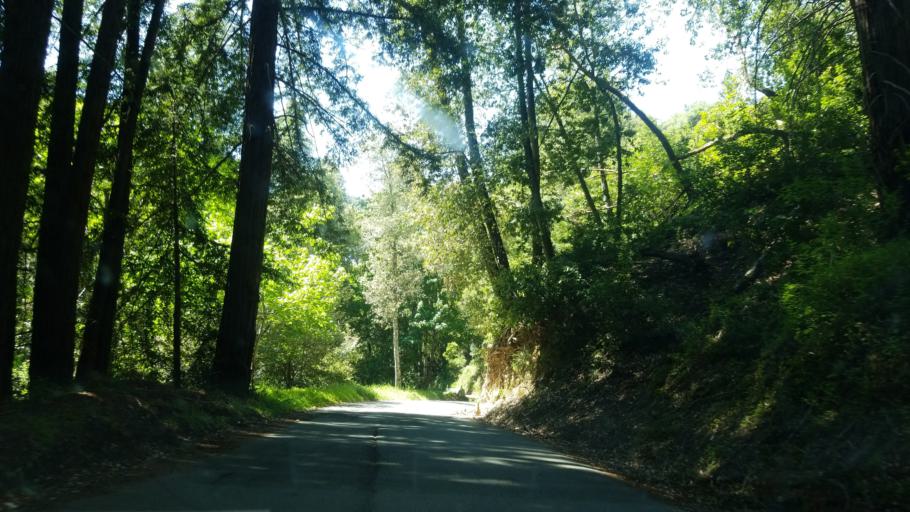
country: US
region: California
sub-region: Santa Cruz County
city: Day Valley
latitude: 37.0552
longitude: -121.8148
